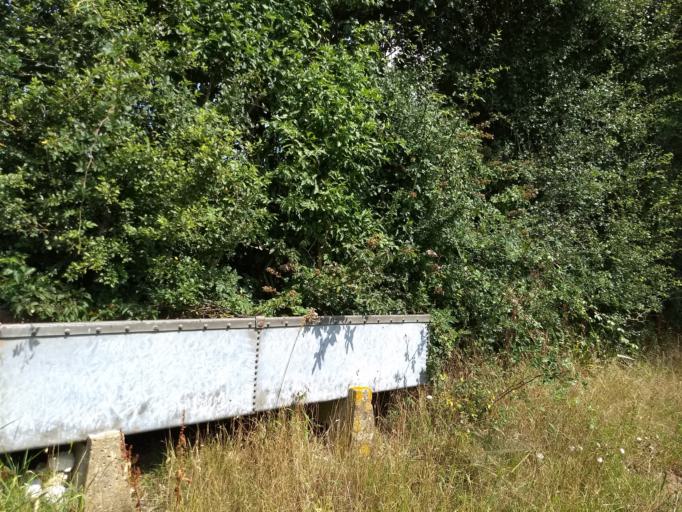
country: GB
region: England
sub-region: Isle of Wight
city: Brading
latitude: 50.6916
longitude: -1.1558
